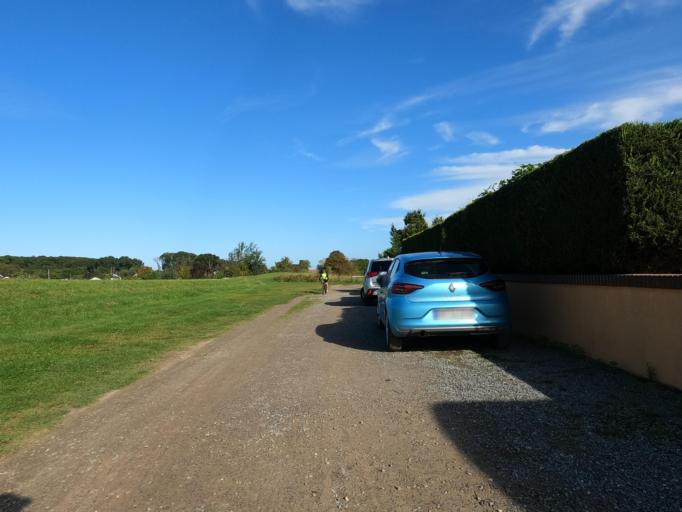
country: DE
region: Schleswig-Holstein
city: Dahme
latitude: 54.2788
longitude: 11.0828
